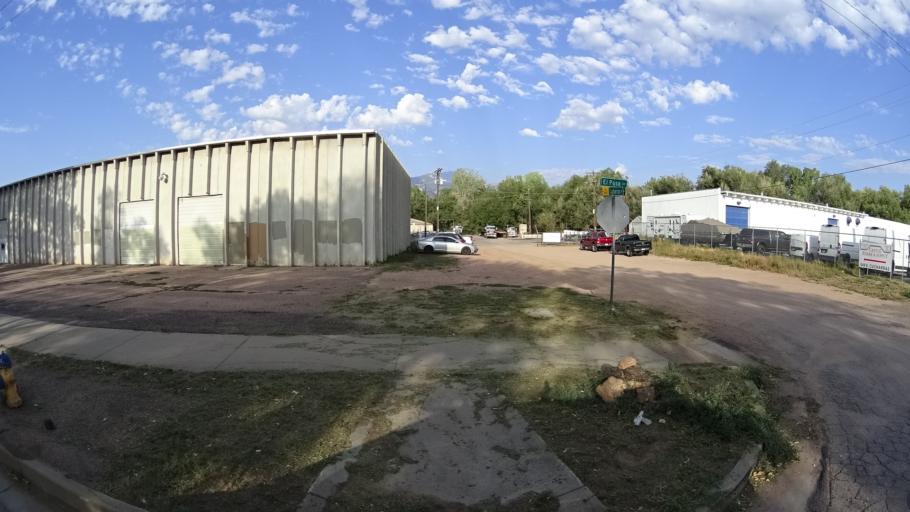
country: US
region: Colorado
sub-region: El Paso County
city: Colorado Springs
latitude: 38.8307
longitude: -104.8131
